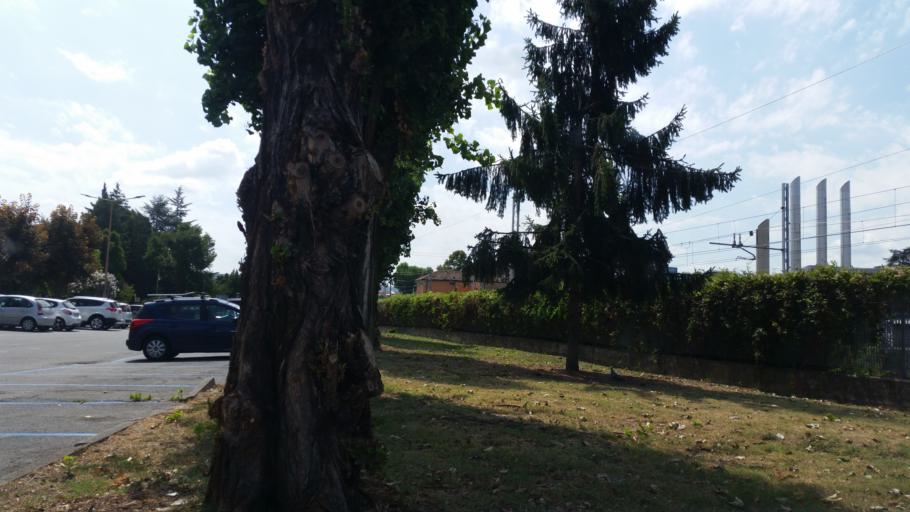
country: IT
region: Piedmont
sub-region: Provincia di Cuneo
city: Alba
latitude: 44.6998
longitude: 8.0292
